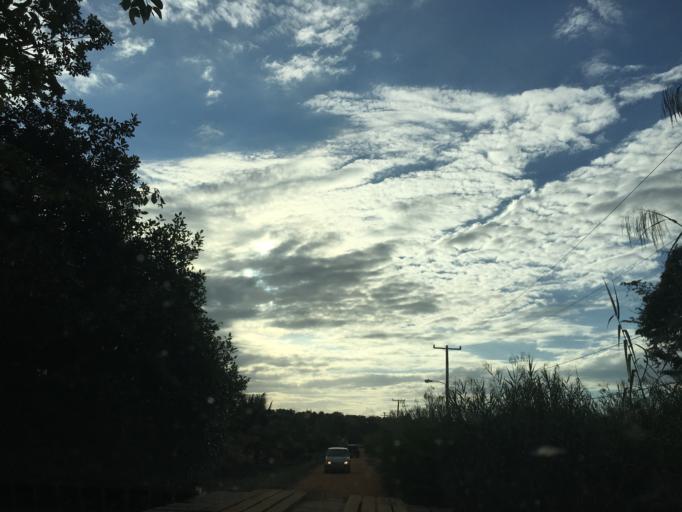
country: BZ
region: Stann Creek
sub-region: Dangriga
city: Dangriga
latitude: 16.8227
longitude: -88.2665
